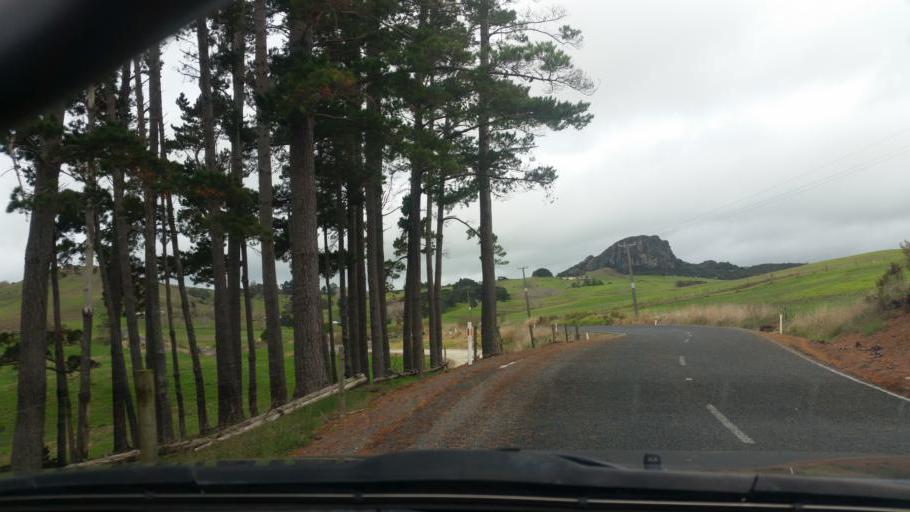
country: NZ
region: Northland
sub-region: Kaipara District
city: Dargaville
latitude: -36.0064
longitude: 173.9674
